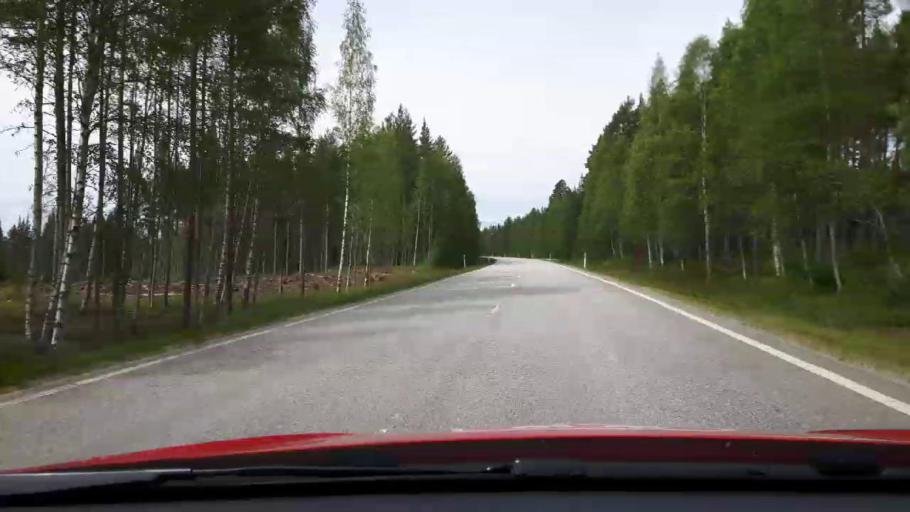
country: SE
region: Jaemtland
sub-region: Harjedalens Kommun
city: Sveg
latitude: 62.1237
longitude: 14.1575
